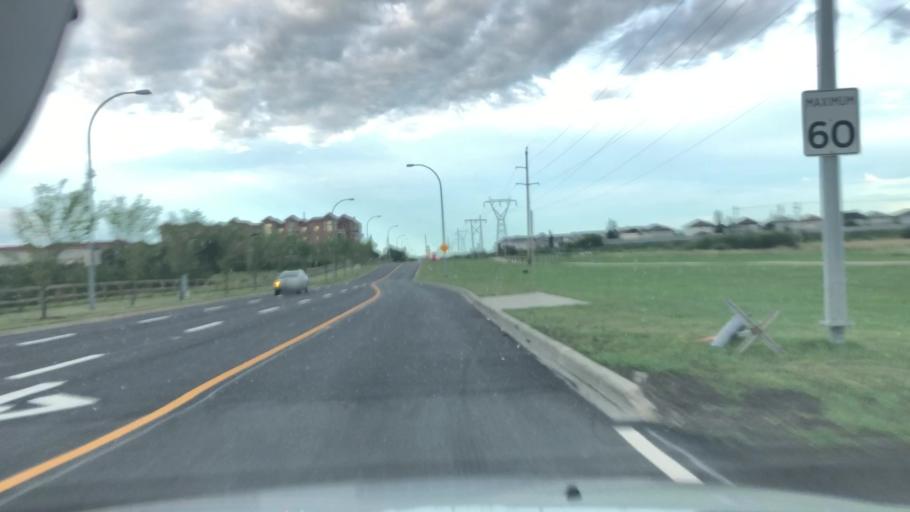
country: CA
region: Alberta
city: St. Albert
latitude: 53.6145
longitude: -113.5690
